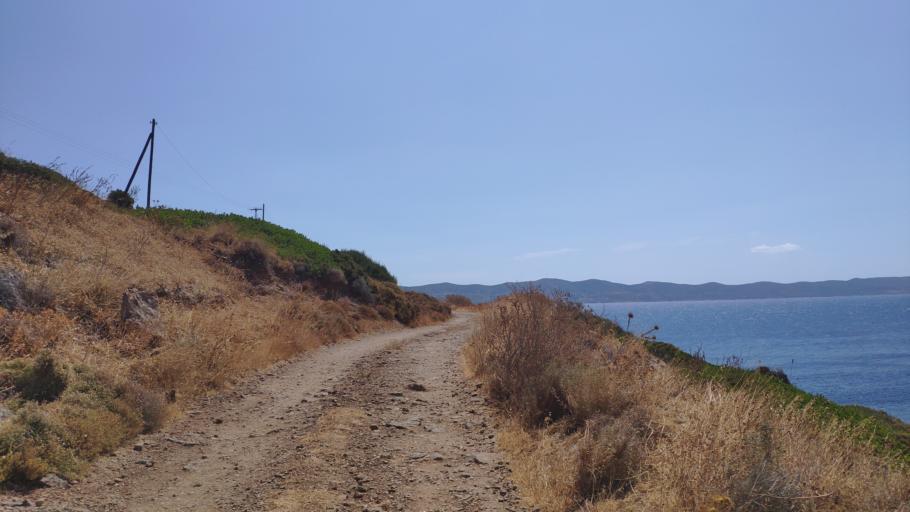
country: GR
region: Attica
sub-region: Nomarchia Anatolikis Attikis
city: Lavrio
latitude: 37.7442
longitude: 24.0763
